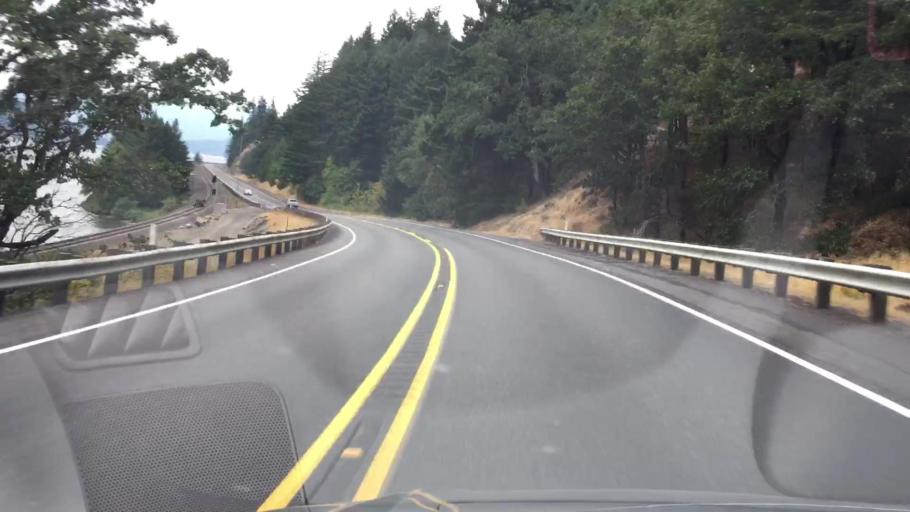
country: US
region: Washington
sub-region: Skamania County
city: Carson
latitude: 45.7025
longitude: -121.7448
